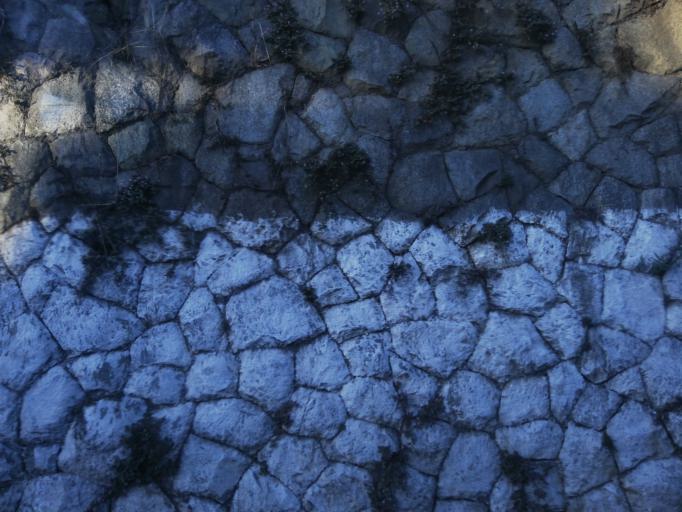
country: PH
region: Cordillera
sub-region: Baguio City
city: Baguio
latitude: 16.4320
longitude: 120.5973
